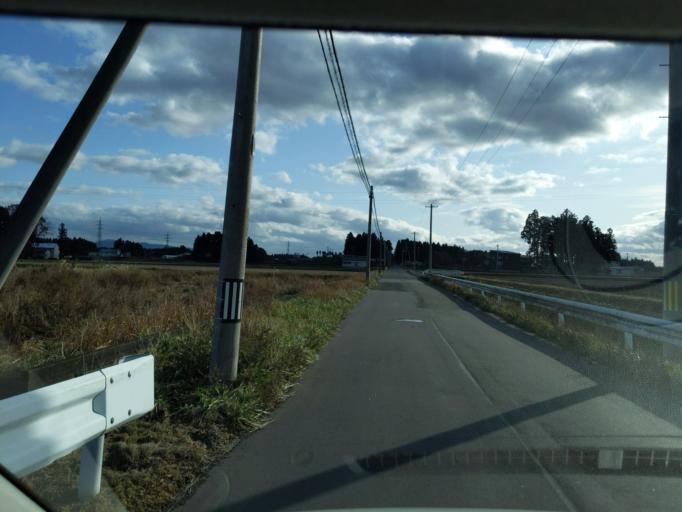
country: JP
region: Iwate
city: Mizusawa
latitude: 39.1320
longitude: 141.0806
